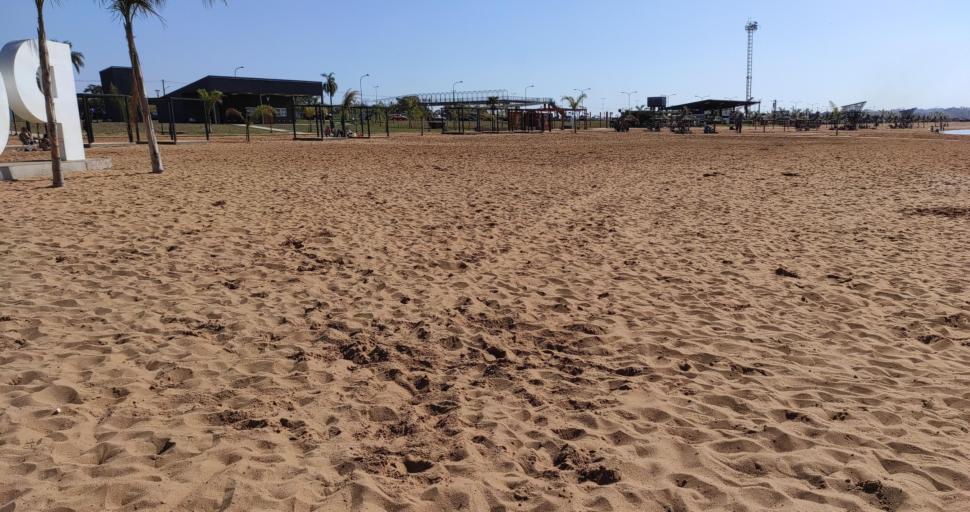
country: AR
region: Misiones
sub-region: Departamento de Capital
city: Posadas
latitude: -27.4201
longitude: -55.8770
